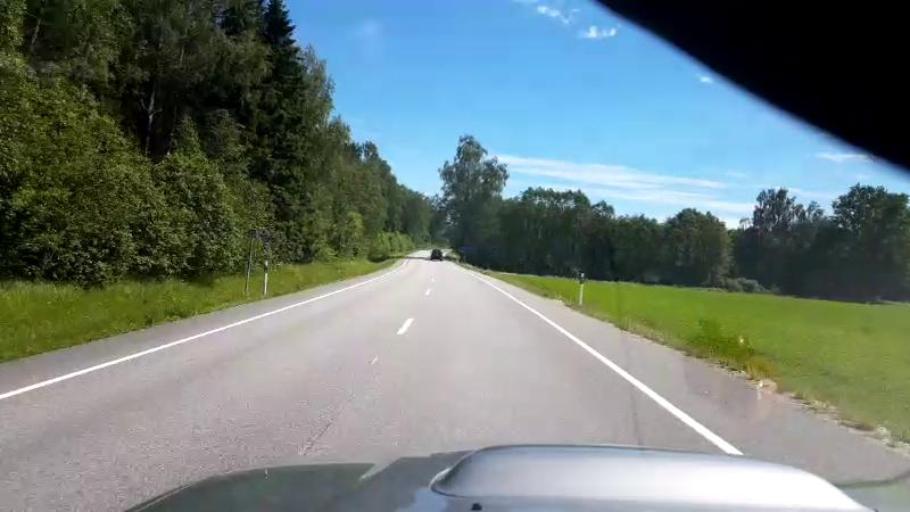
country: EE
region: Jaervamaa
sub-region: Jaerva-Jaani vald
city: Jarva-Jaani
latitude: 59.0113
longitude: 25.9215
